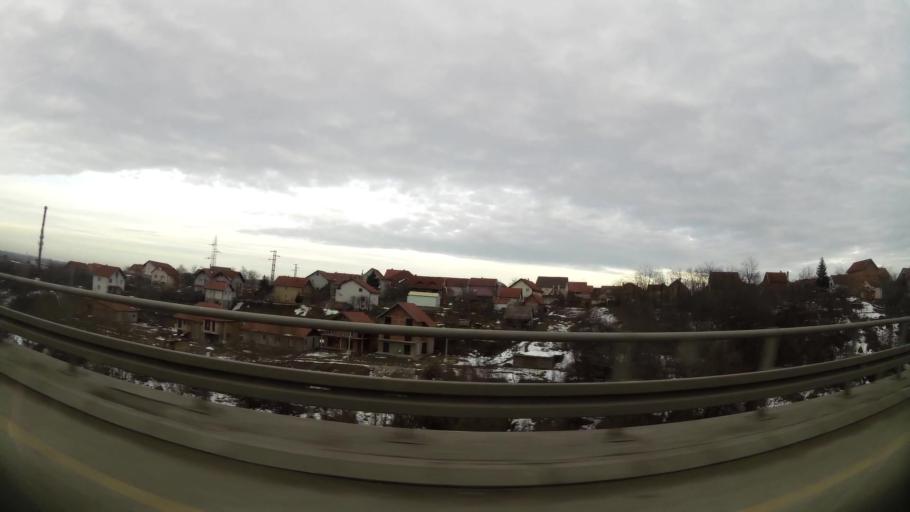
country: RS
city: Ostruznica
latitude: 44.7203
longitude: 20.3594
